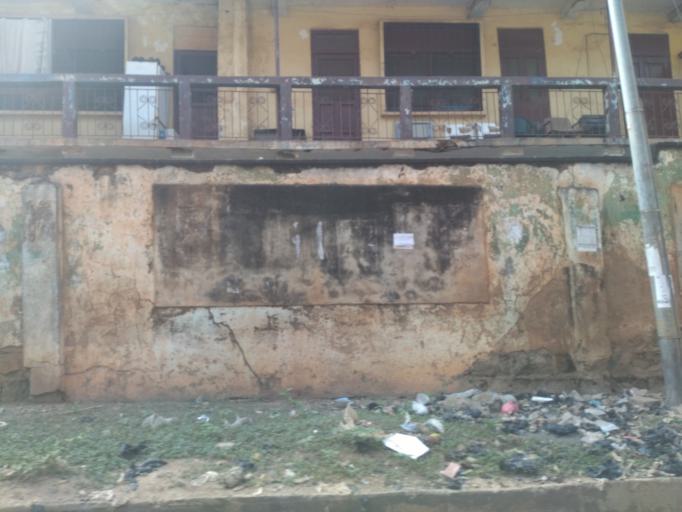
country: GH
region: Ashanti
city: Kumasi
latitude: 6.6951
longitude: -1.6090
